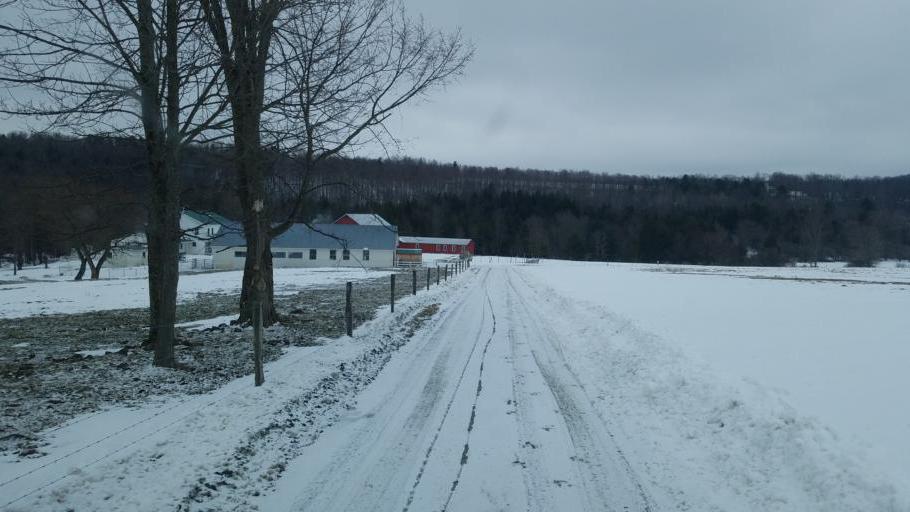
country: US
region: Pennsylvania
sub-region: Tioga County
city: Elkland
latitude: 42.0802
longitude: -77.4521
